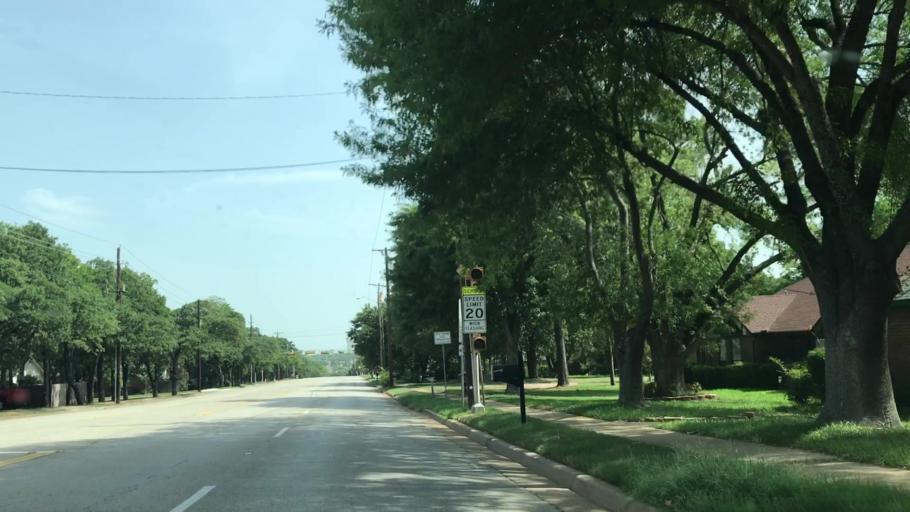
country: US
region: Texas
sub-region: Tarrant County
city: Euless
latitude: 32.8573
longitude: -97.0824
